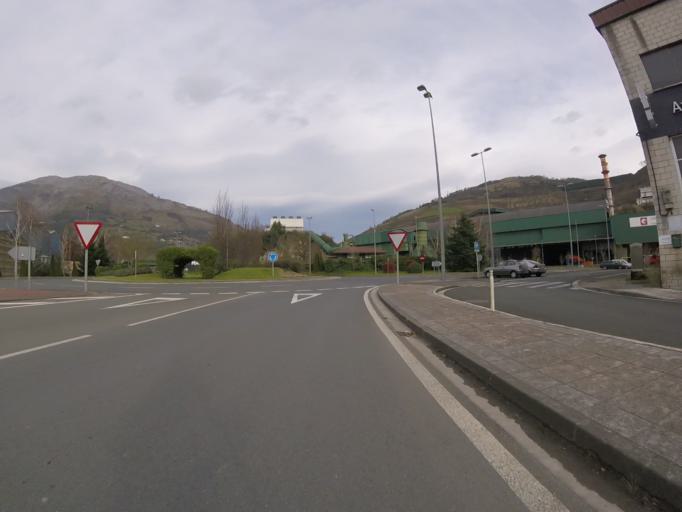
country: ES
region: Basque Country
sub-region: Provincia de Guipuzcoa
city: Azpeitia
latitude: 43.1798
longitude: -2.2592
